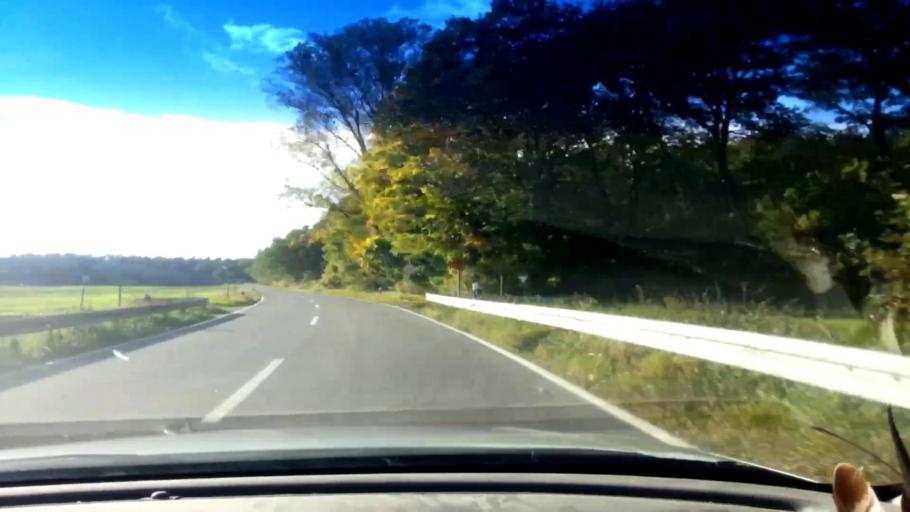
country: DE
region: Bavaria
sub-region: Upper Franconia
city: Strullendorf
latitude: 49.8566
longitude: 10.9906
